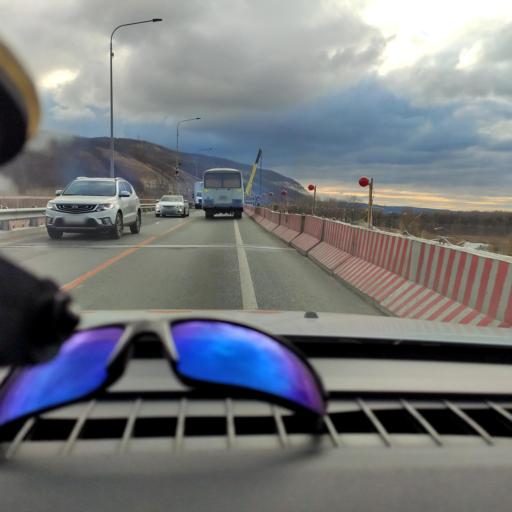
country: RU
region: Samara
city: Volzhskiy
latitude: 53.4130
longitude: 50.1353
